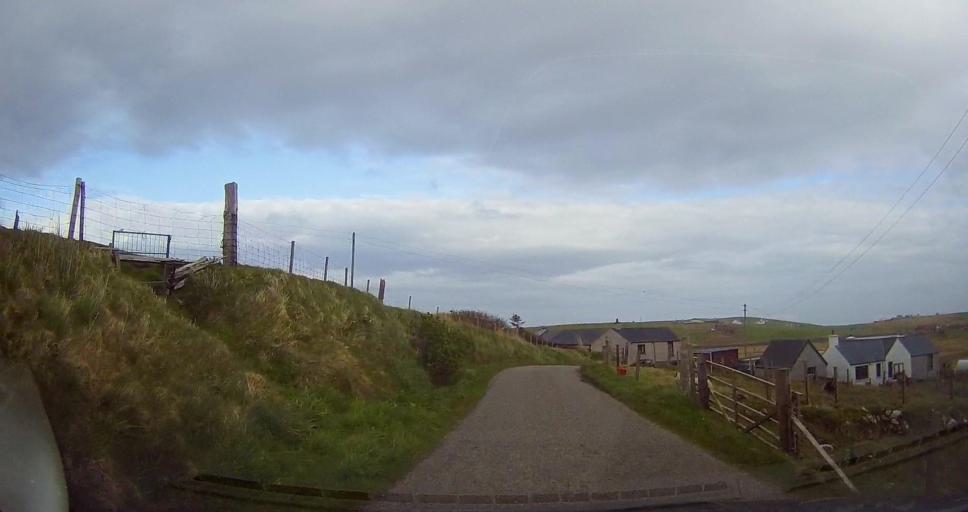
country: GB
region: Scotland
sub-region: Shetland Islands
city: Sandwick
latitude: 60.0483
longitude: -1.2165
